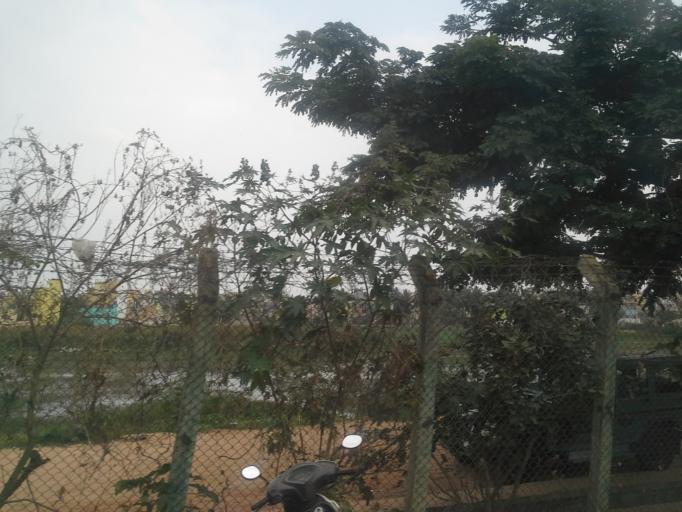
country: IN
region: Karnataka
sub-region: Bangalore Urban
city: Bangalore
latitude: 13.0051
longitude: 77.6927
